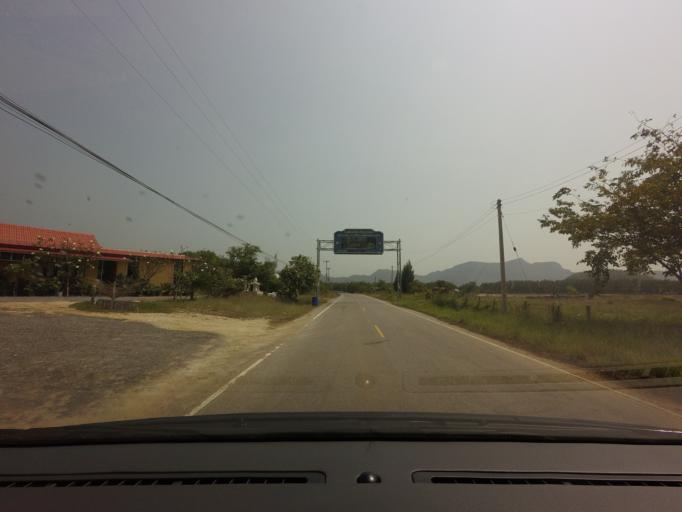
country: TH
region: Prachuap Khiri Khan
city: Sam Roi Yot
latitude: 12.1948
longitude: 99.9870
